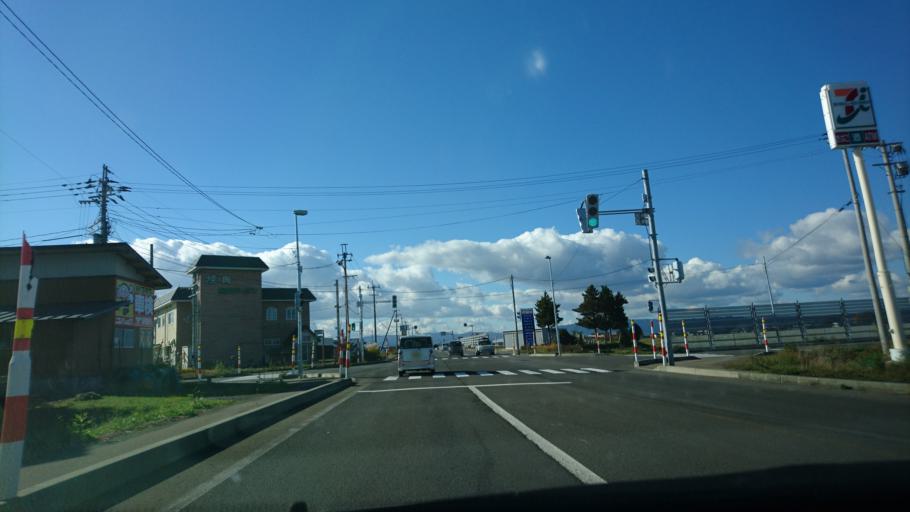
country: JP
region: Akita
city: Yokotemachi
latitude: 39.2688
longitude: 140.4930
